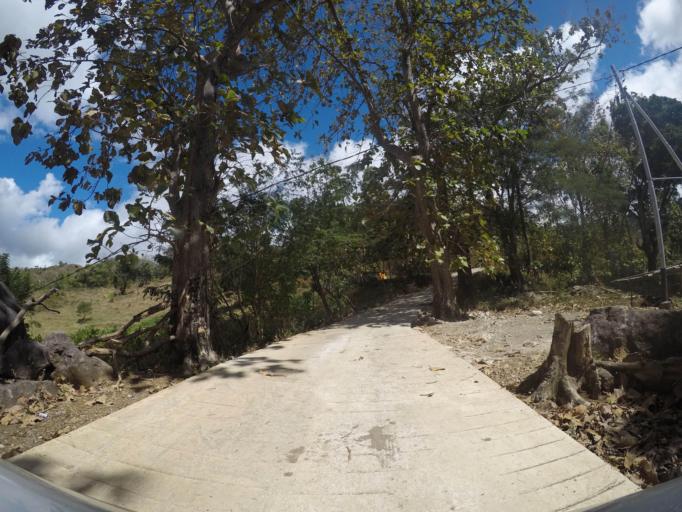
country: TL
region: Lautem
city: Lospalos
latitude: -8.5335
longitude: 126.7997
